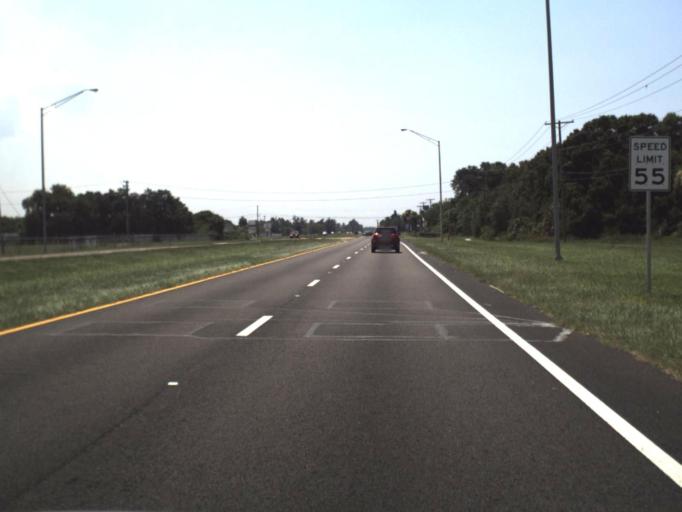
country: US
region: Florida
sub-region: Hillsborough County
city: Apollo Beach
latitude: 27.7624
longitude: -82.3974
